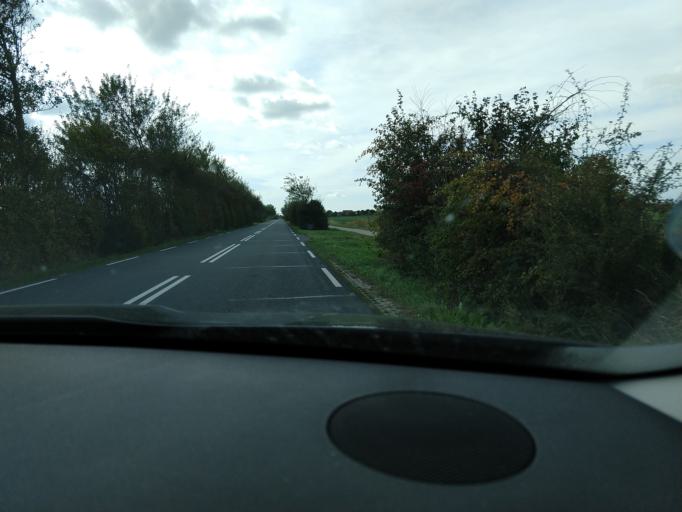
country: NL
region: Zeeland
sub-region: Gemeente Middelburg
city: Middelburg
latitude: 51.5238
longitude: 3.5366
